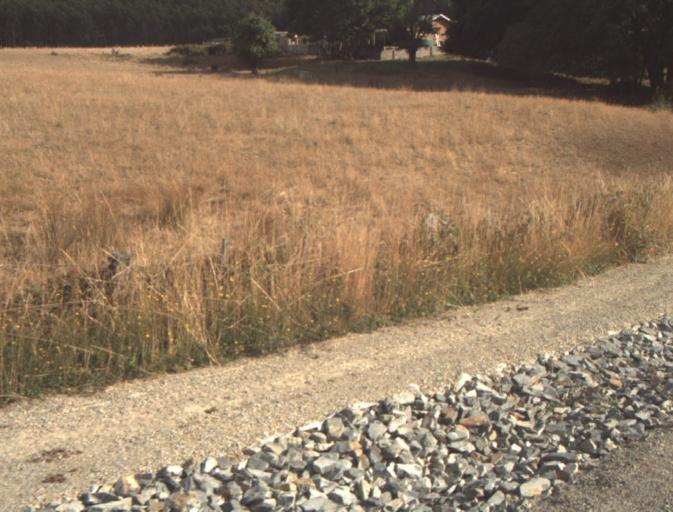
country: AU
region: Tasmania
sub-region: Launceston
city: Mayfield
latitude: -41.1768
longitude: 147.2283
